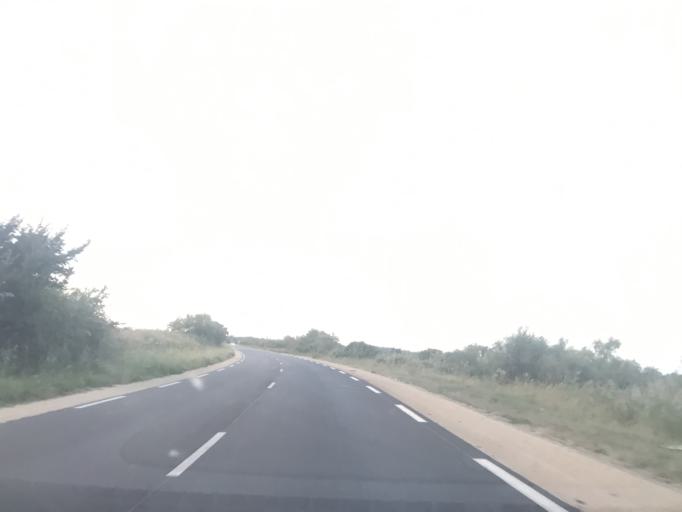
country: FR
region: Provence-Alpes-Cote d'Azur
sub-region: Departement des Bouches-du-Rhone
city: Saintes-Maries-de-la-Mer
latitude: 43.5404
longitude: 4.4012
